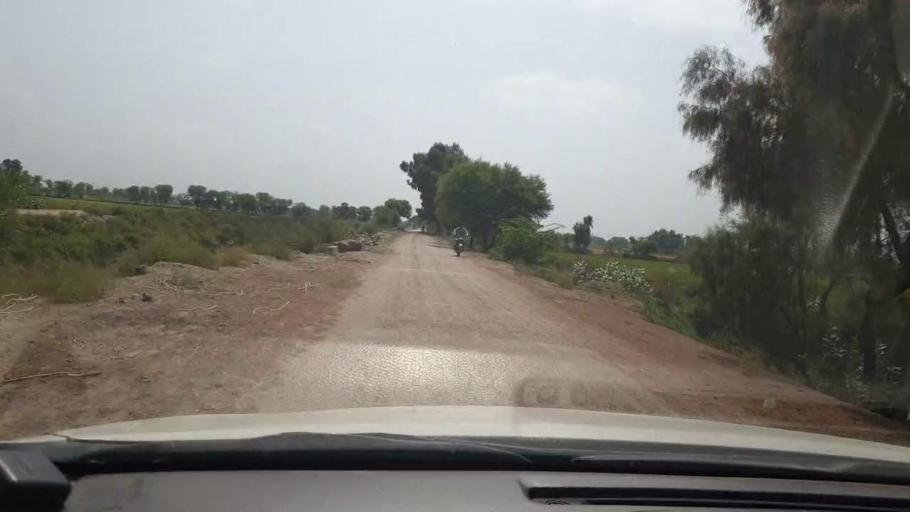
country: PK
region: Sindh
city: Shikarpur
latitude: 28.0089
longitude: 68.5709
